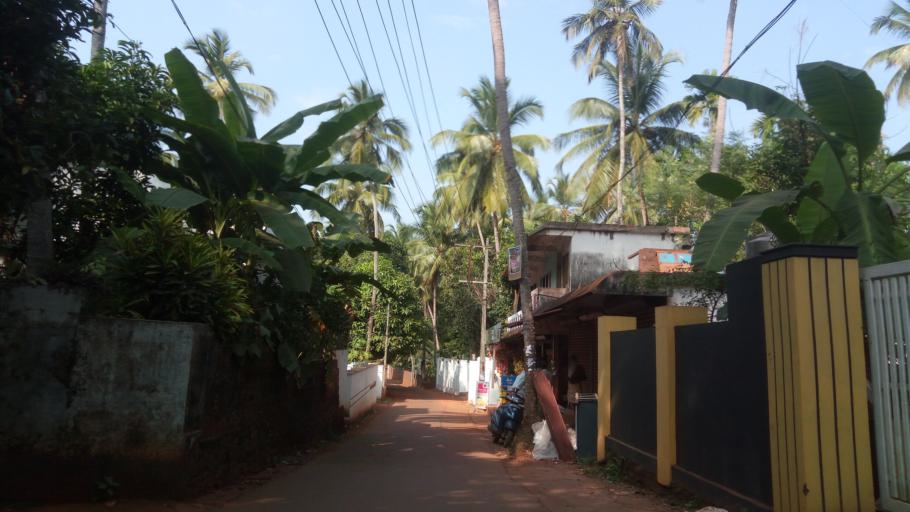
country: IN
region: Kerala
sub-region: Malappuram
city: Malappuram
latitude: 10.9946
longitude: 75.9996
